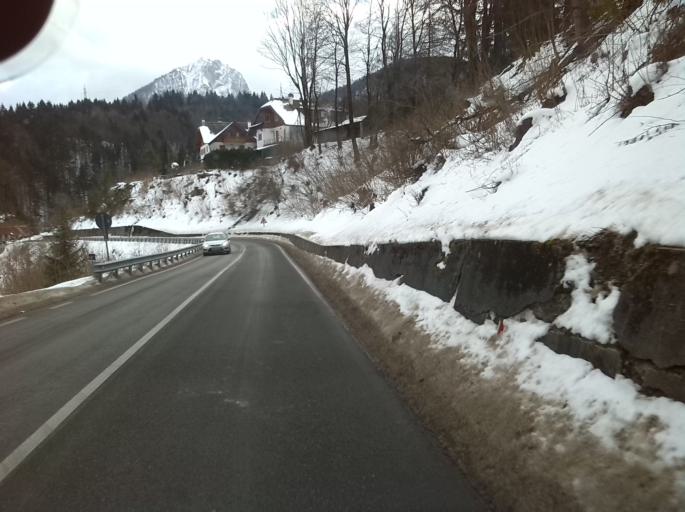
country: IT
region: Friuli Venezia Giulia
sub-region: Provincia di Udine
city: Tarvisio
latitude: 46.5034
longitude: 13.5904
